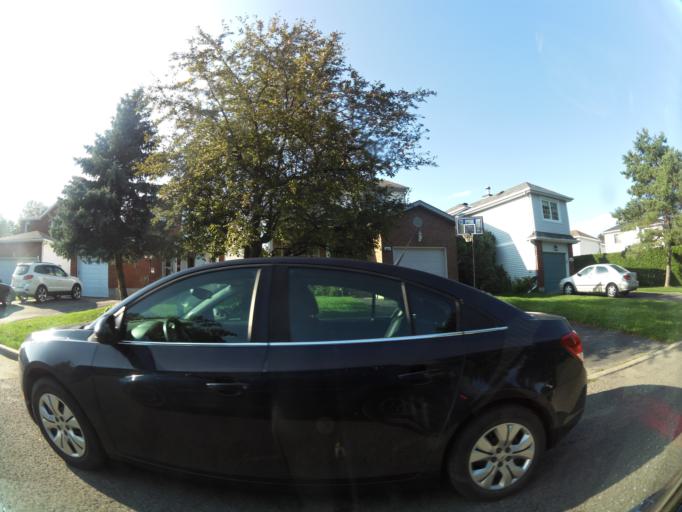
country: CA
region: Ontario
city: Clarence-Rockland
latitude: 45.4804
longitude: -75.4788
